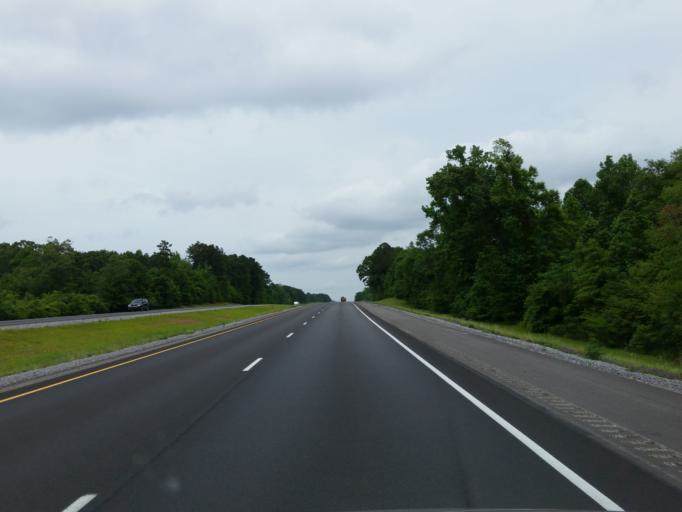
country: US
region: Mississippi
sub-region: Jones County
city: Sharon
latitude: 31.8762
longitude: -89.0438
